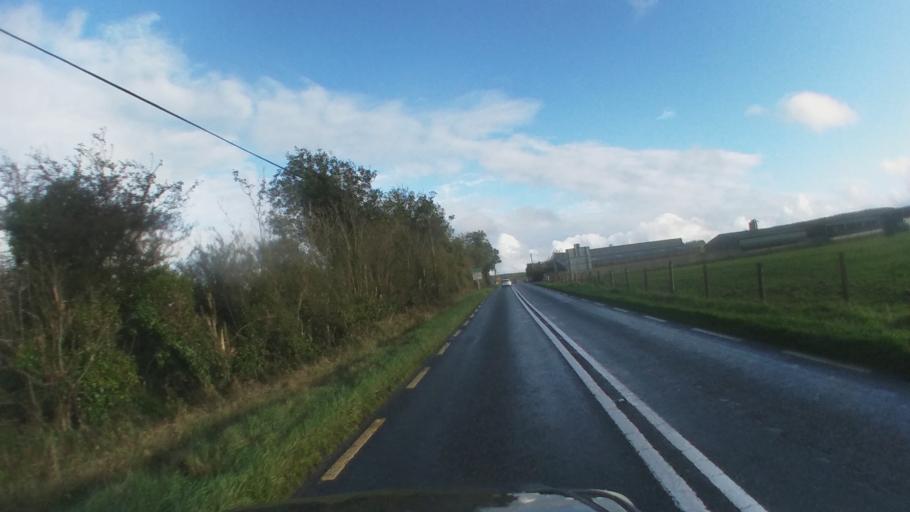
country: IE
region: Connaught
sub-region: Roscommon
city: Castlerea
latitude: 53.8314
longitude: -8.3701
